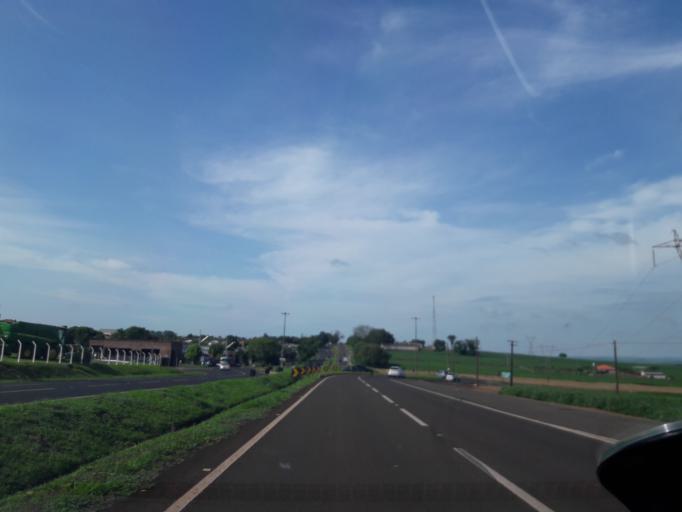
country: BR
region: Parana
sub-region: Paicandu
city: Paicandu
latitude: -23.6043
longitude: -52.0832
